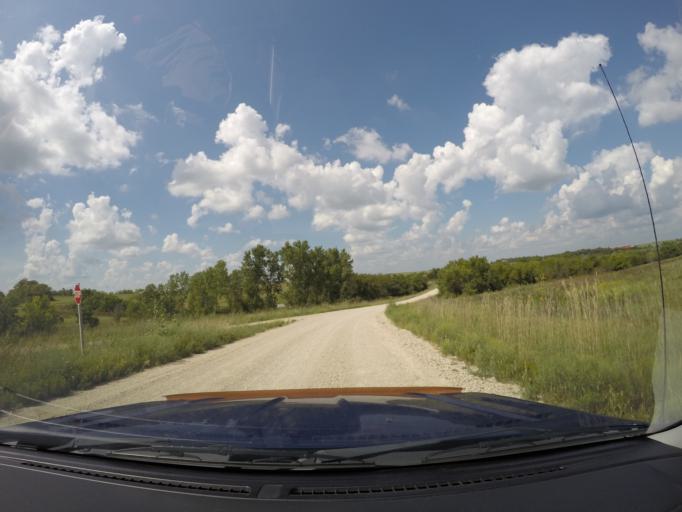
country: US
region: Kansas
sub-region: Wabaunsee County
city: Alma
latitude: 39.0587
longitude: -96.3534
